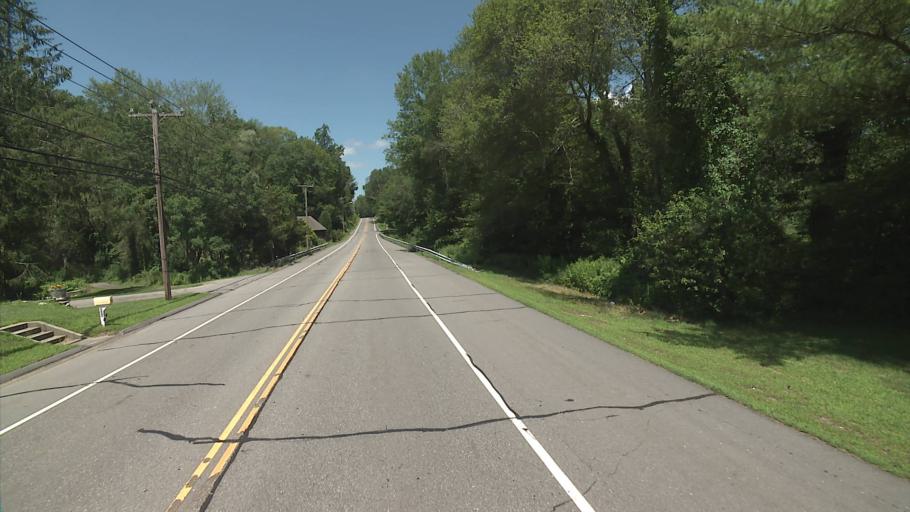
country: US
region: Connecticut
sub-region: Windham County
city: Plainfield Village
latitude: 41.6988
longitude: -72.0012
